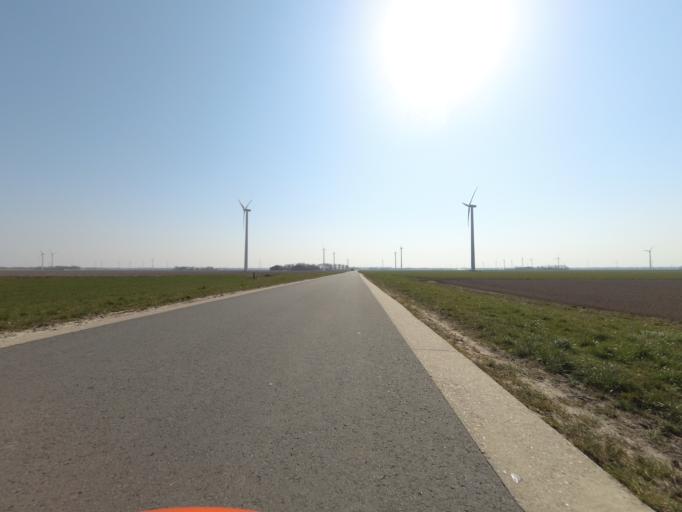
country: NL
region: Utrecht
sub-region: Gemeente Bunschoten
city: Spakenburg
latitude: 52.3411
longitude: 5.3787
